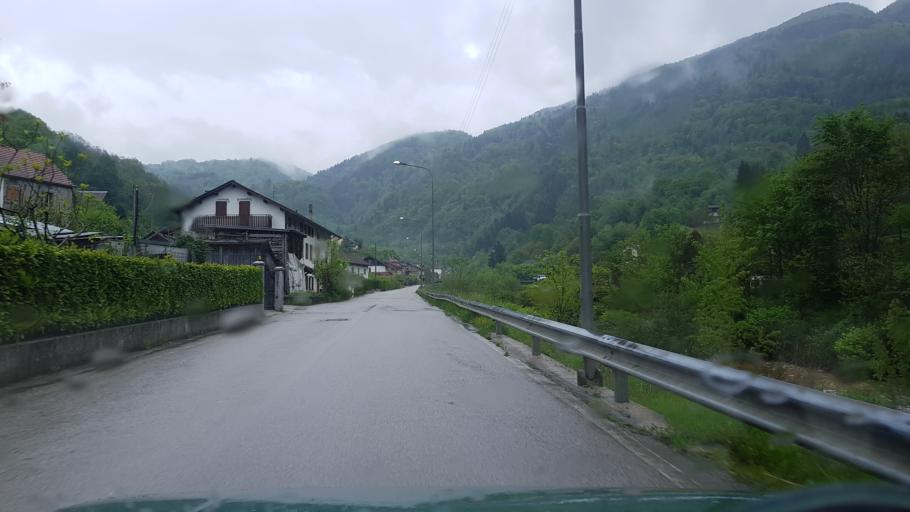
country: IT
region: Veneto
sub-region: Provincia di Belluno
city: Farra d'Alpago
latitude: 46.1165
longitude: 12.3649
